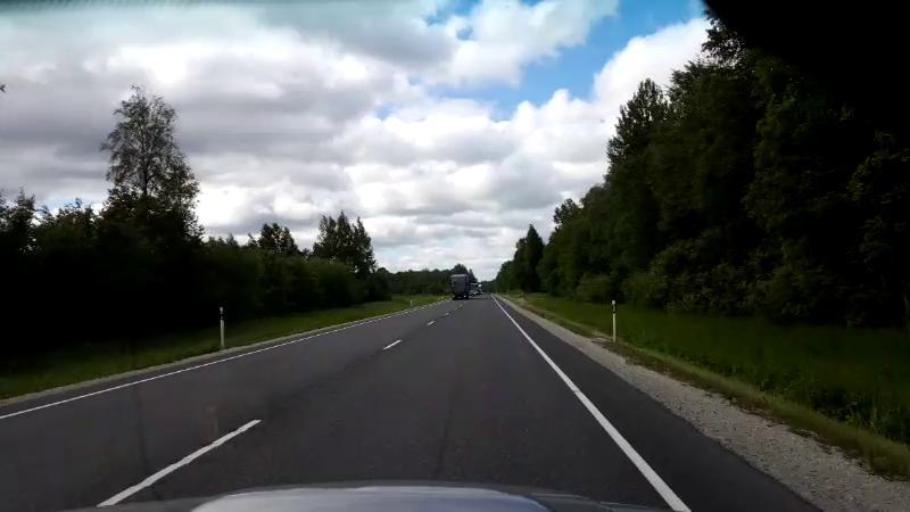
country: EE
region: Raplamaa
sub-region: Maerjamaa vald
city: Marjamaa
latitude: 58.8342
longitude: 24.4200
